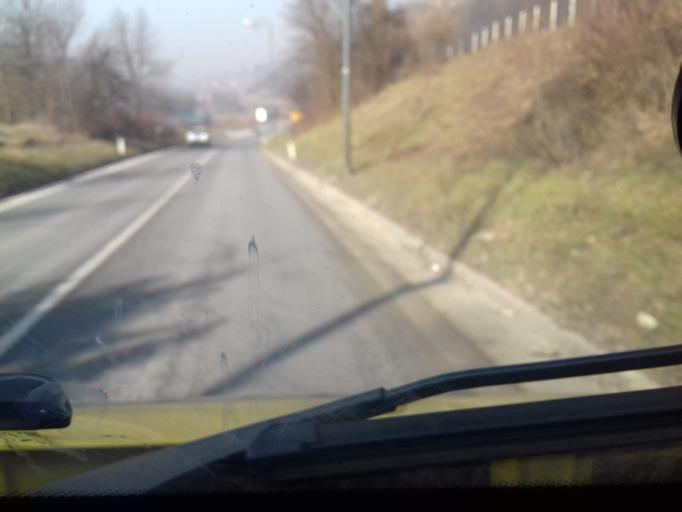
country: BA
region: Federation of Bosnia and Herzegovina
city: Vogosca
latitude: 43.9057
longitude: 18.3287
